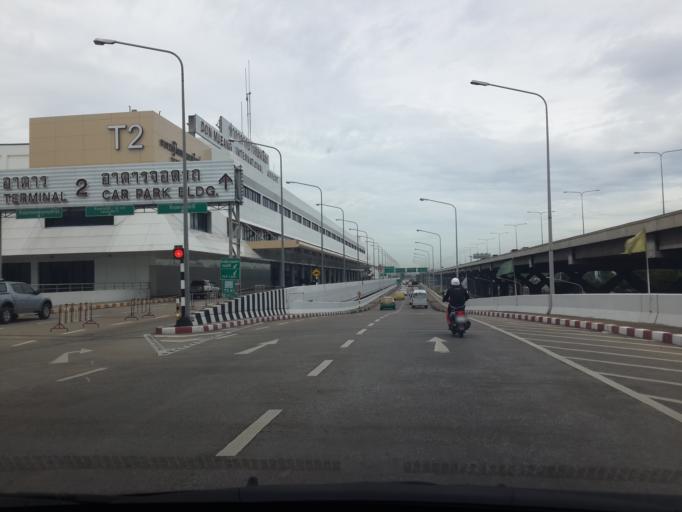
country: TH
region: Bangkok
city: Don Mueang
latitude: 13.9194
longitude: 100.6015
